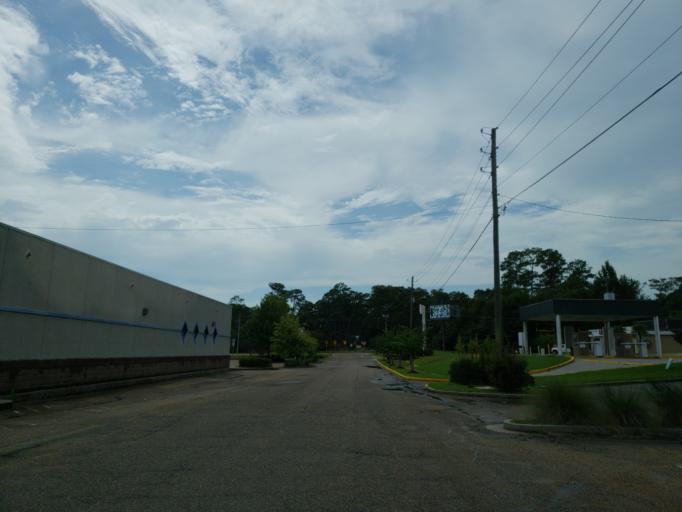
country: US
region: Mississippi
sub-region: Forrest County
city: Hattiesburg
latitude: 31.3120
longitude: -89.3197
